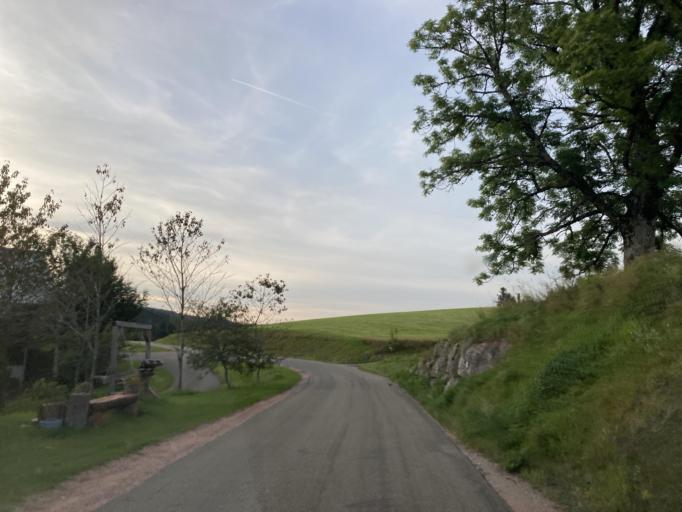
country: DE
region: Baden-Wuerttemberg
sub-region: Freiburg Region
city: Schonwald im Schwarzwald
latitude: 48.1001
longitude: 8.1739
